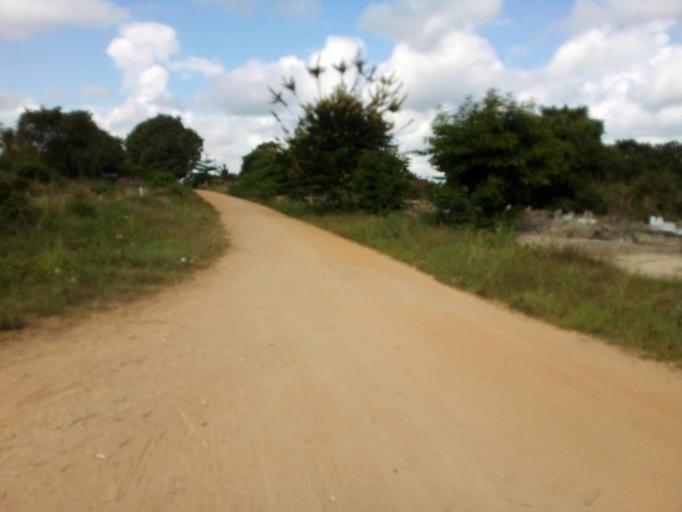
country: MZ
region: Zambezia
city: Quelimane
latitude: -17.5546
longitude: 36.6982
